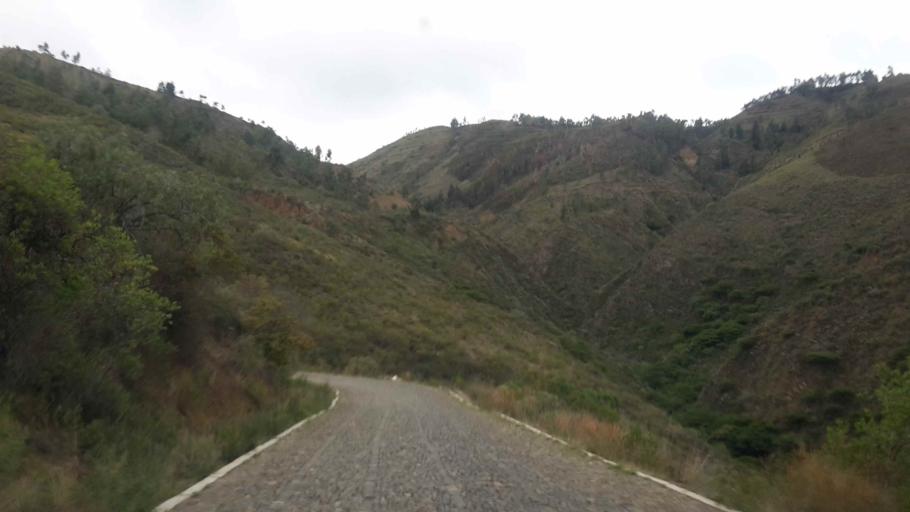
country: BO
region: Cochabamba
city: Cochabamba
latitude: -17.3682
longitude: -66.0615
